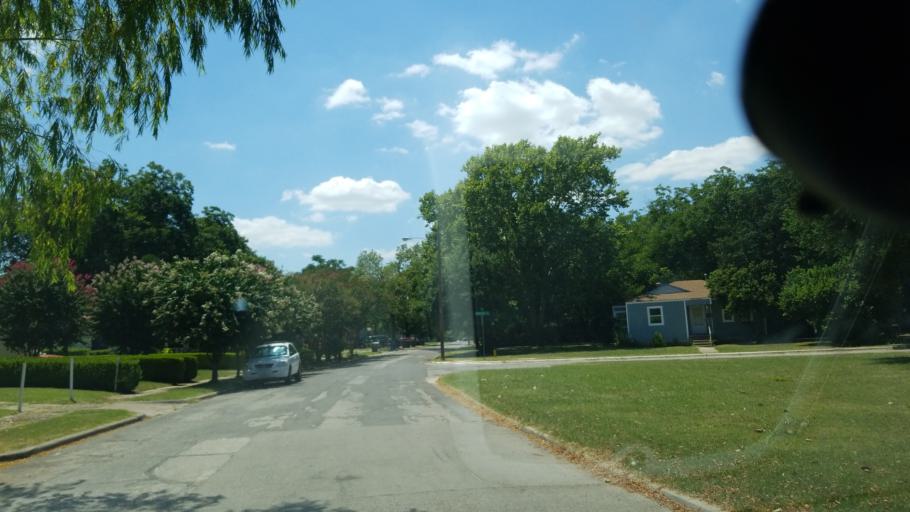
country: US
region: Texas
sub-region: Dallas County
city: Cockrell Hill
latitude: 32.7147
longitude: -96.8419
